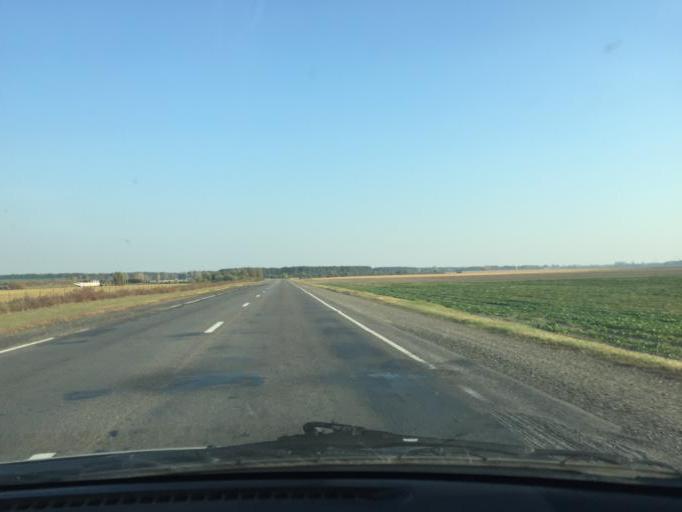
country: BY
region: Brest
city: Davyd-Haradok
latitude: 52.2520
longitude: 27.0603
